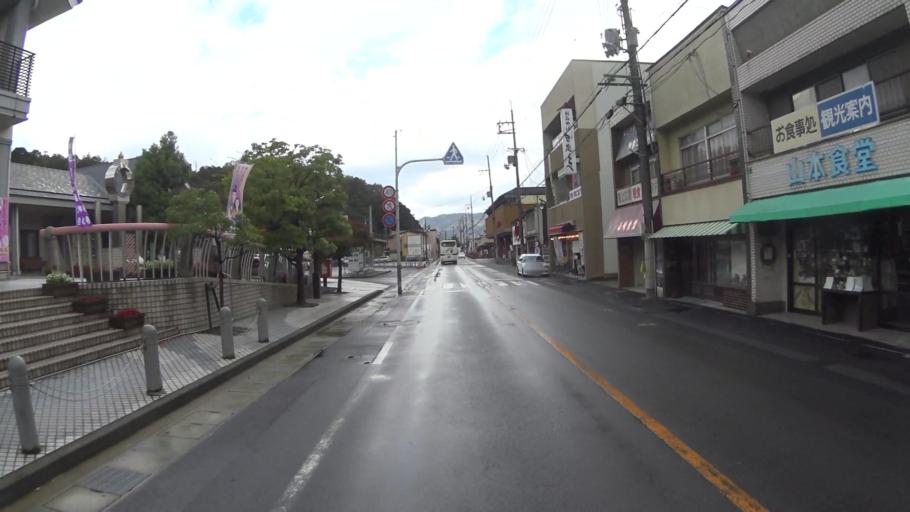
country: JP
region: Kyoto
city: Miyazu
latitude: 35.5576
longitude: 135.1820
